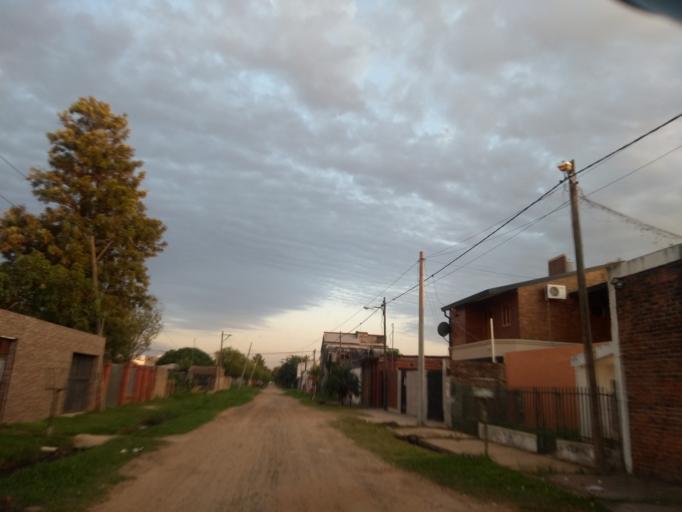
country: AR
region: Chaco
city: Resistencia
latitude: -27.4761
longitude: -58.9771
